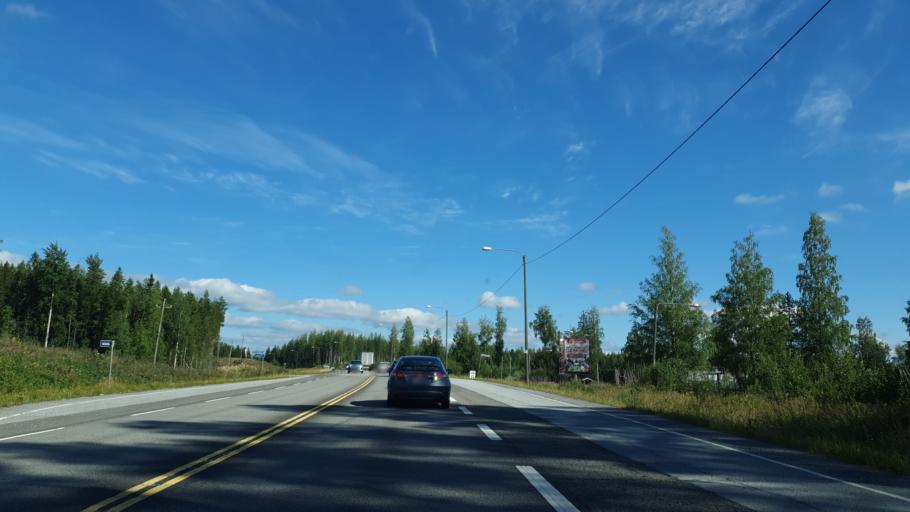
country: FI
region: Central Finland
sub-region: Jyvaeskylae
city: Toivakka
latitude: 62.2463
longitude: 26.0373
